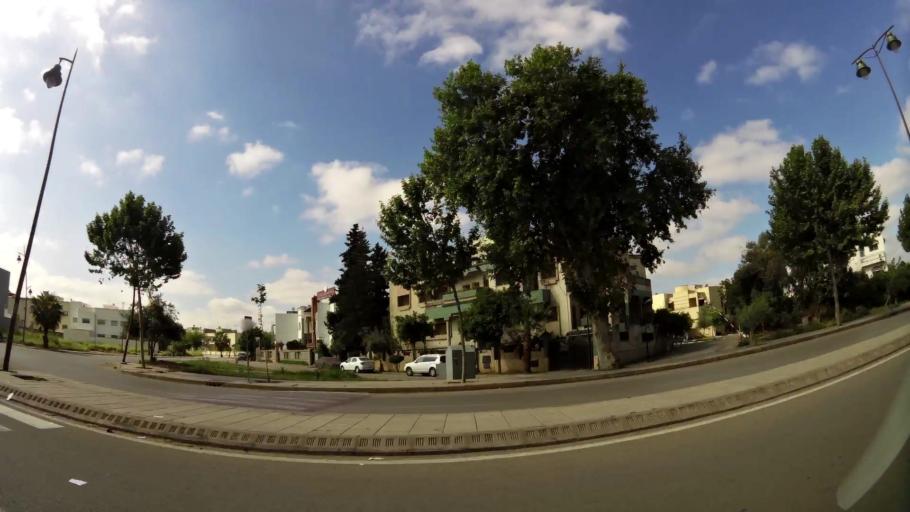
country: MA
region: Fes-Boulemane
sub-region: Fes
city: Fes
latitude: 34.0264
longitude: -5.0245
